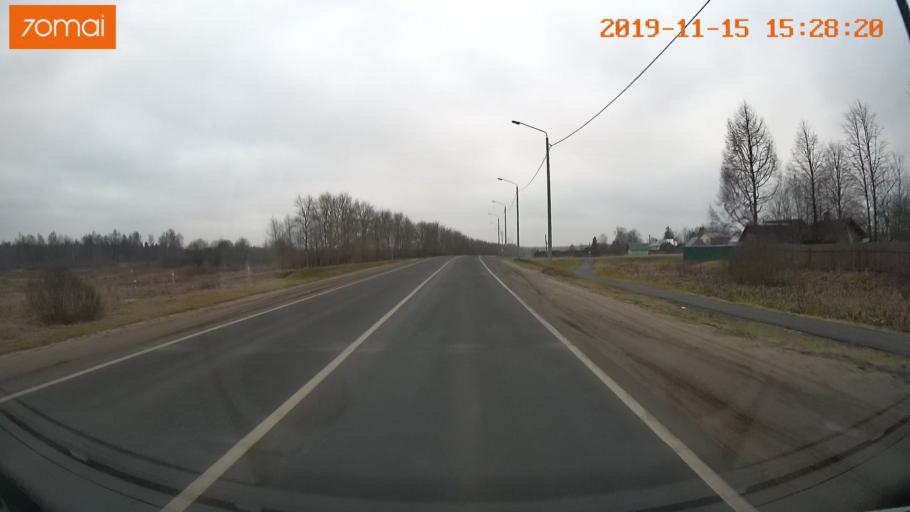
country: RU
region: Jaroslavl
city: Danilov
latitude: 58.1332
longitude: 40.1360
